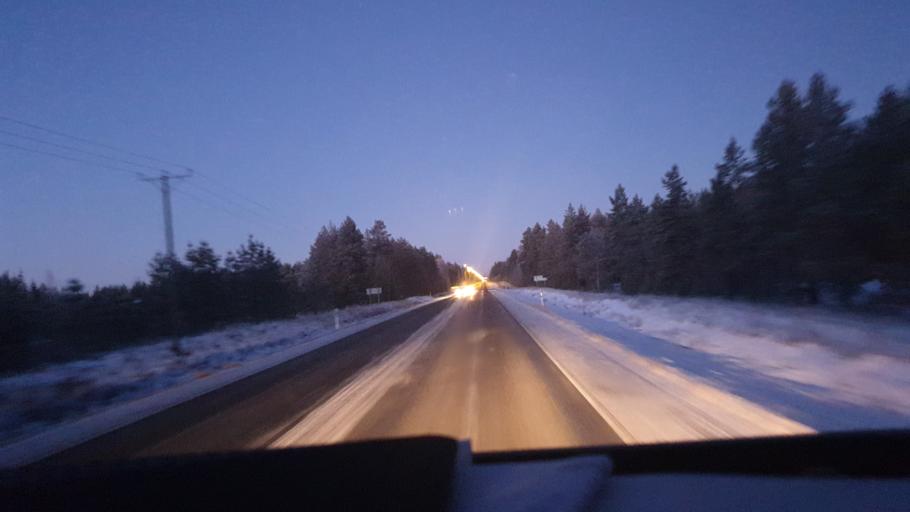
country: FI
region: Northern Ostrobothnia
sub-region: Raahe
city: Siikajoki
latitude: 64.6921
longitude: 24.6544
